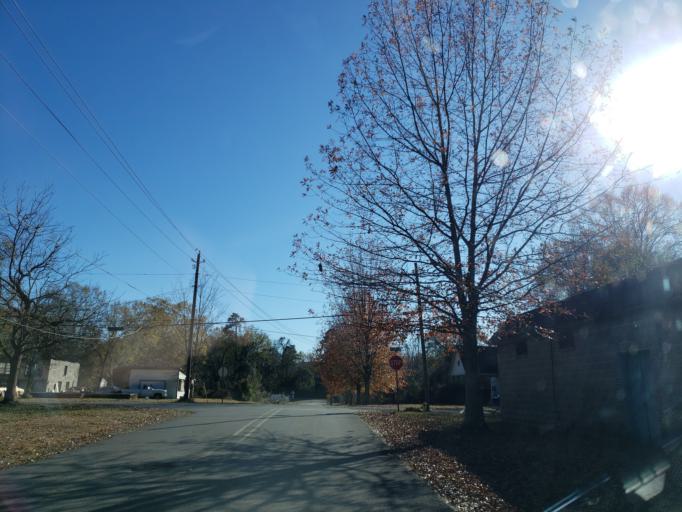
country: US
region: Mississippi
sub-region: Forrest County
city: Hattiesburg
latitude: 31.3336
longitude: -89.2955
